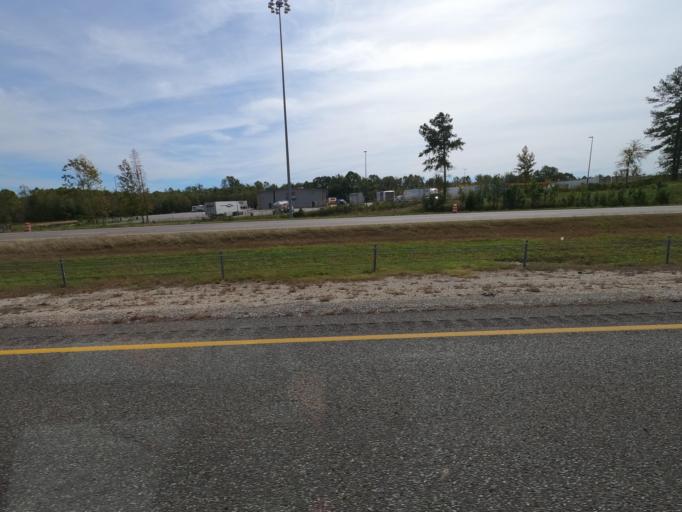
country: US
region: Tennessee
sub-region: Decatur County
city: Parsons
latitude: 35.8417
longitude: -88.0842
